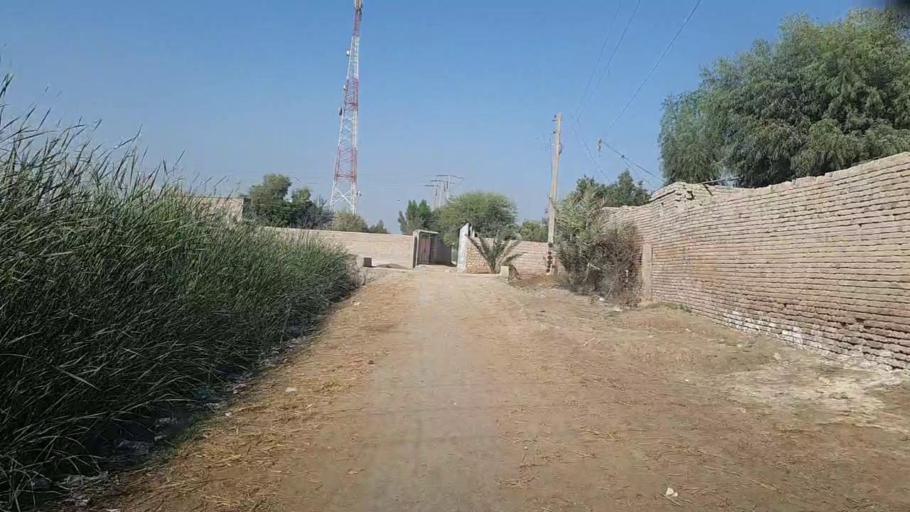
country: PK
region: Sindh
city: Tangwani
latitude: 28.2380
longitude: 68.9294
